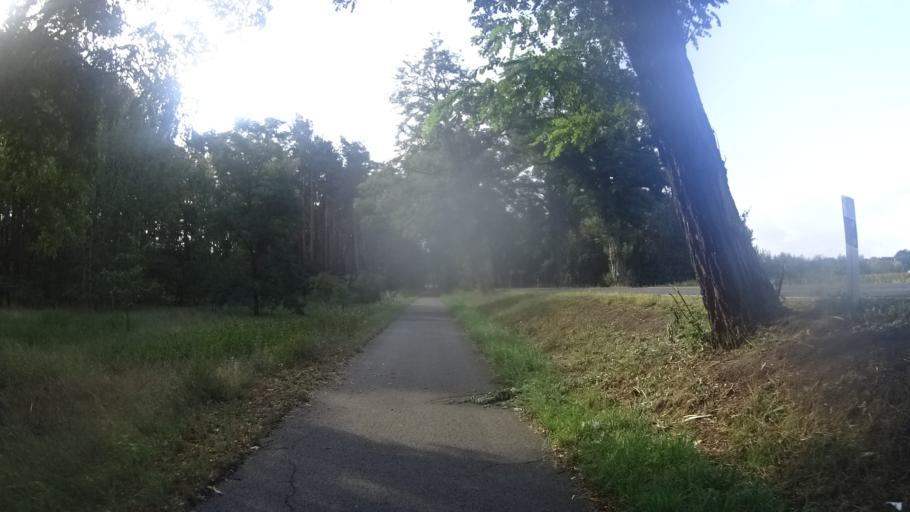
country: DE
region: Brandenburg
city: Wittenberge
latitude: 53.0138
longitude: 11.7068
